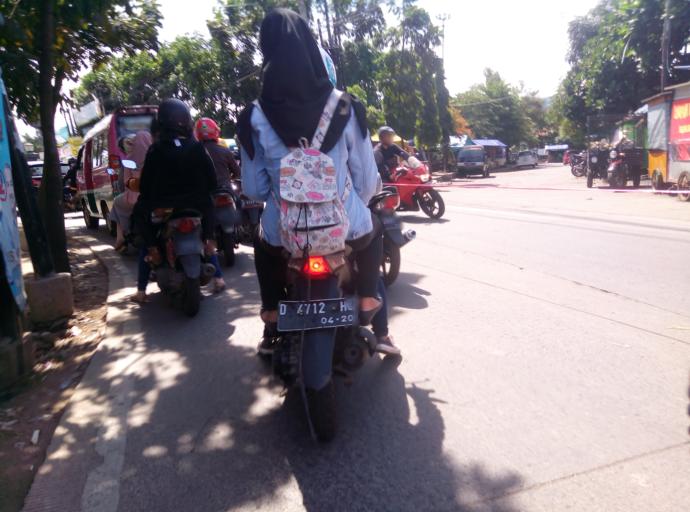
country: ID
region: West Java
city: Bandung
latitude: -6.8931
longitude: 107.6358
